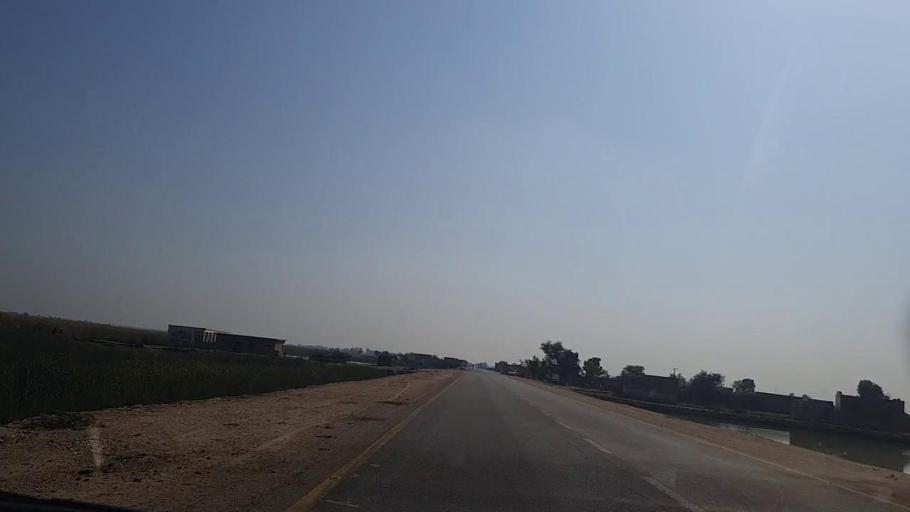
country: PK
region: Sindh
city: Sakrand
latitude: 26.0757
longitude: 68.4046
